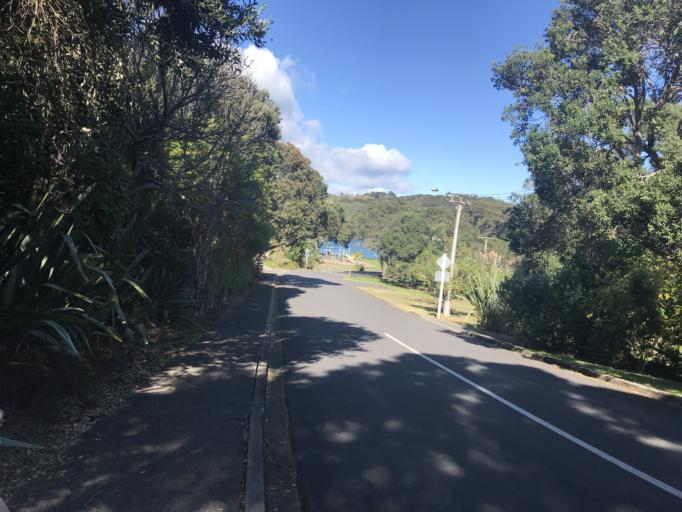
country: NZ
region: Auckland
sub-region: Auckland
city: Warkworth
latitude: -36.2998
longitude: 174.7993
